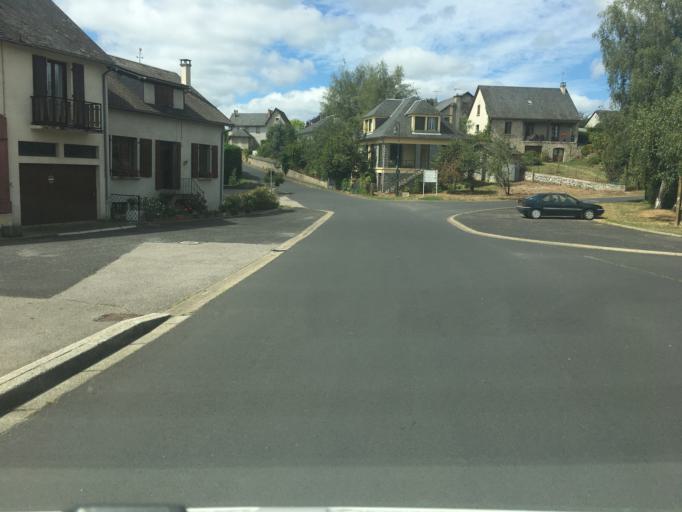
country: FR
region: Limousin
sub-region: Departement de la Correze
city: Neuvic
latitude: 45.4147
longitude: 2.3333
